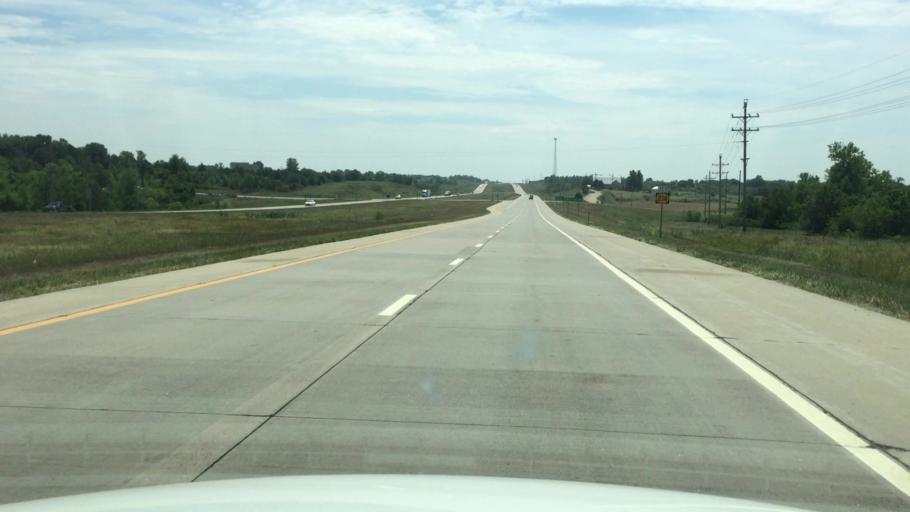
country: US
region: Kansas
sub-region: Jackson County
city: Holton
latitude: 39.2632
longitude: -95.7201
